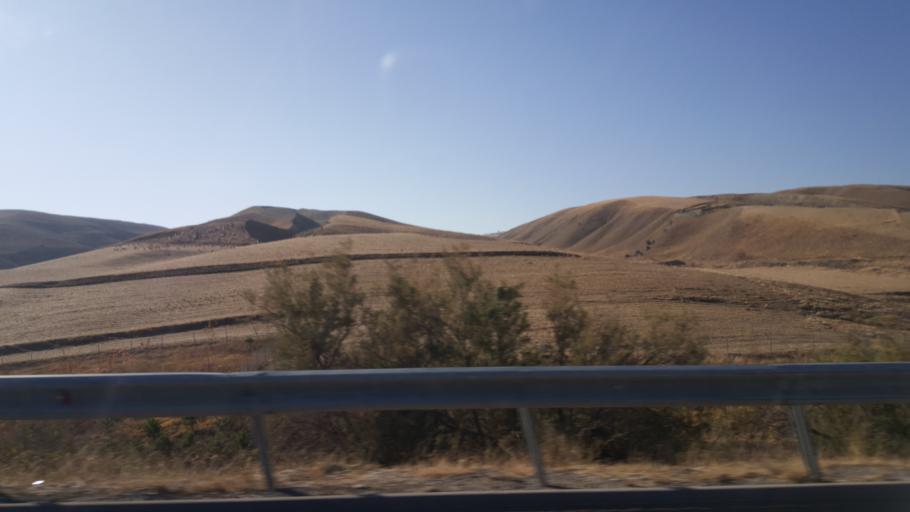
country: TR
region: Ankara
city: Mamak
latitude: 39.8717
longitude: 32.9277
